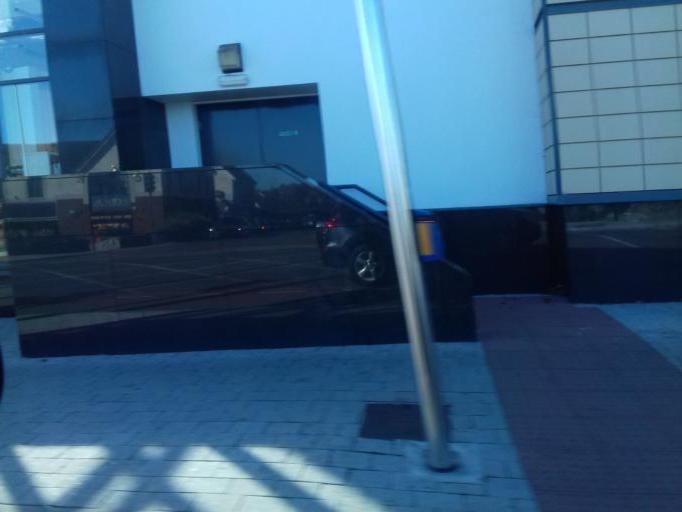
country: IE
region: Leinster
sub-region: An Mhi
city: Ashbourne
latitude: 53.5130
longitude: -6.3998
